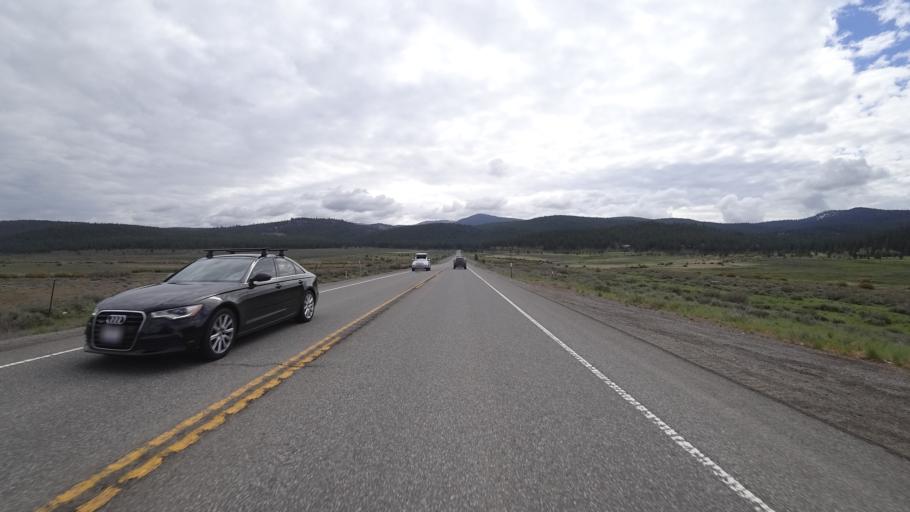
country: US
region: California
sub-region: Nevada County
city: Truckee
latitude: 39.3030
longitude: -120.1266
